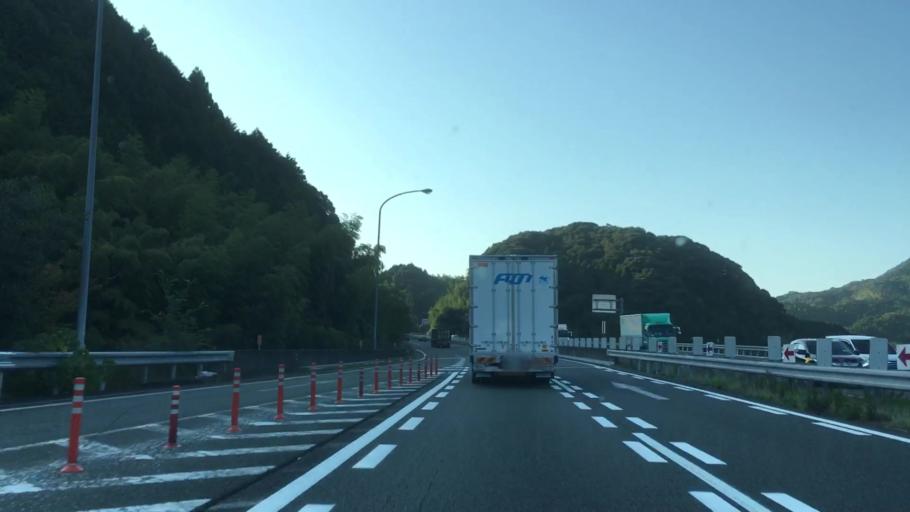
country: JP
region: Yamaguchi
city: Onoda
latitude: 34.1092
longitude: 131.1389
